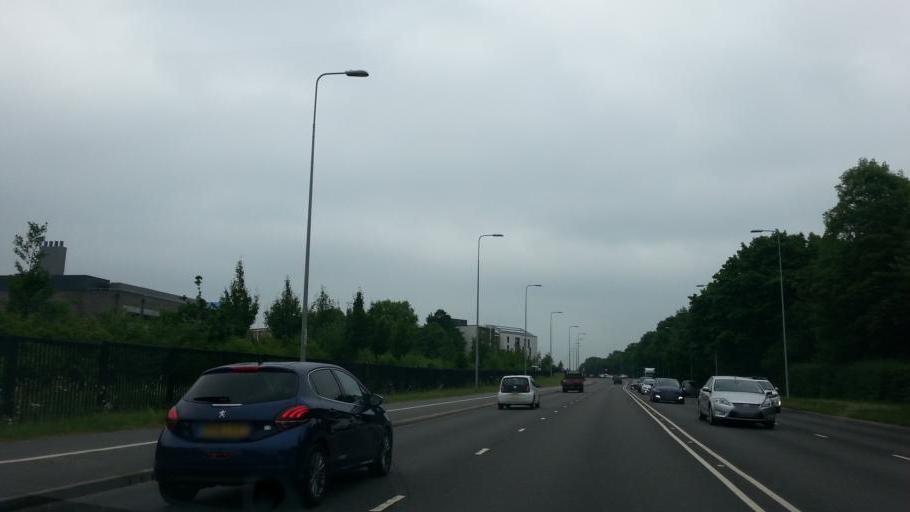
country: GB
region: England
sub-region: Nottinghamshire
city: Ruddington
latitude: 52.9092
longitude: -1.1847
